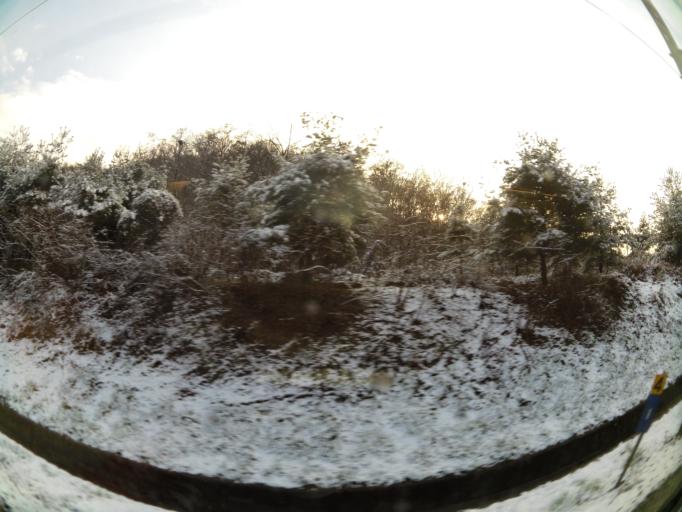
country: KR
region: Daejeon
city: Songgang-dong
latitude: 36.3818
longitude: 127.4176
